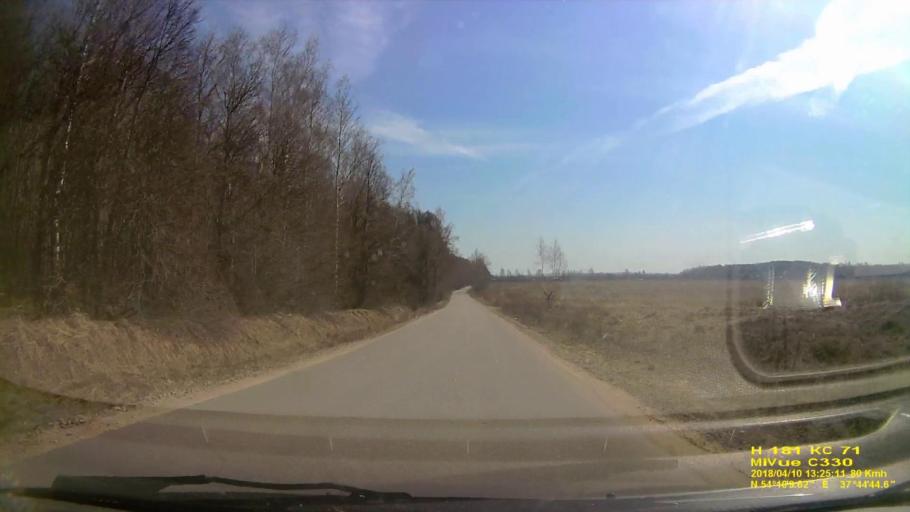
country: RU
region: Tula
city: Bolokhovo
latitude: 54.1693
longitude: 37.7458
